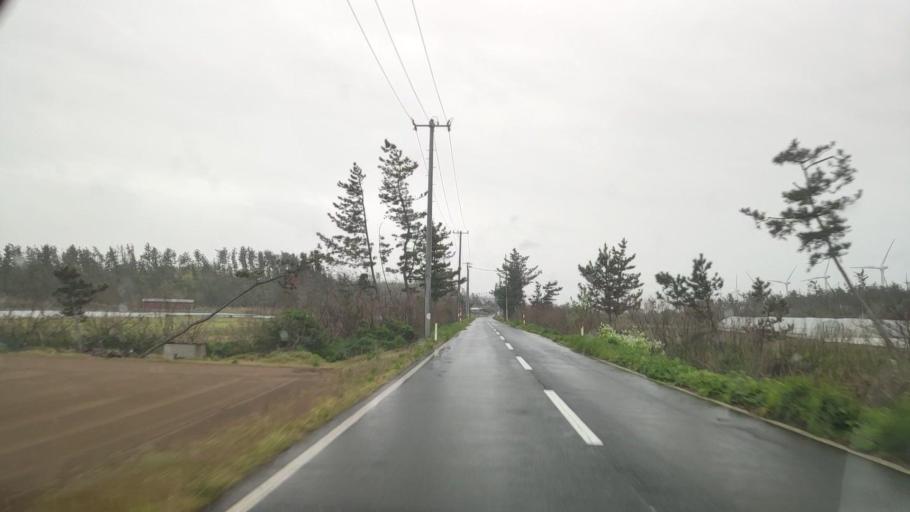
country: JP
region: Akita
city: Noshiromachi
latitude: 40.0930
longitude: 139.9619
